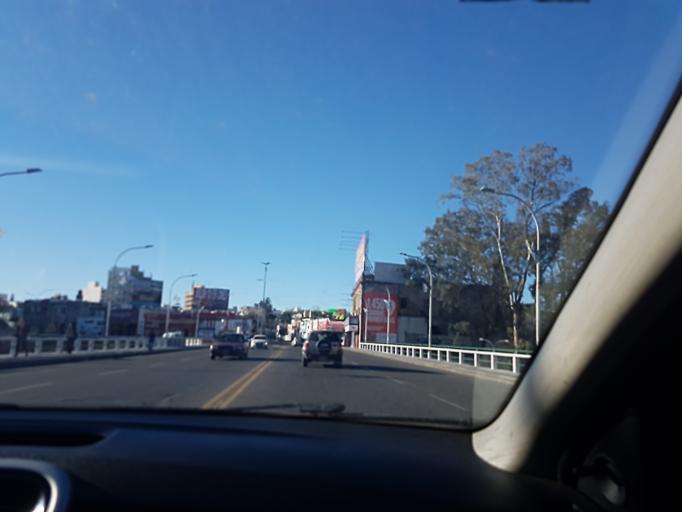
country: AR
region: Cordoba
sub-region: Departamento de Capital
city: Cordoba
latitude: -31.4063
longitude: -64.1939
